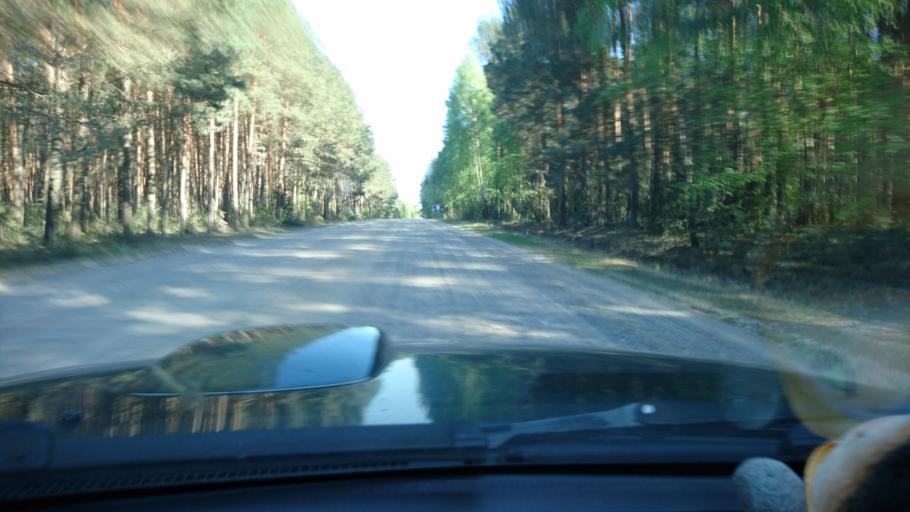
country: BY
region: Brest
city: Zhabinka
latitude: 52.3824
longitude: 24.1170
